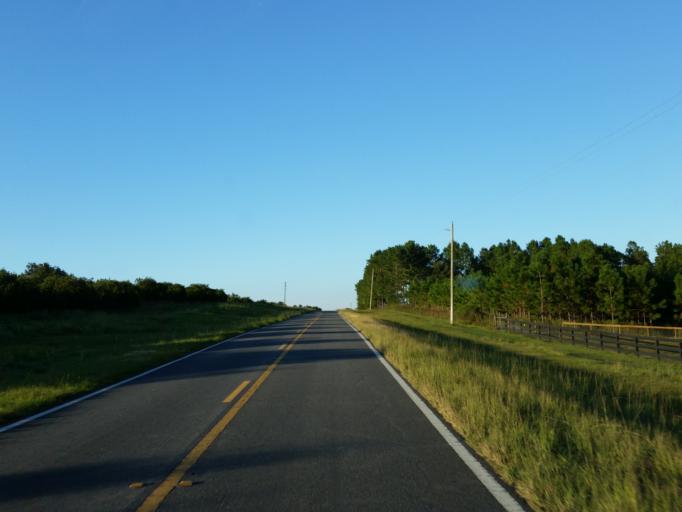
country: US
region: Florida
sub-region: Hernando County
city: Hill 'n Dale
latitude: 28.4426
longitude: -82.2698
